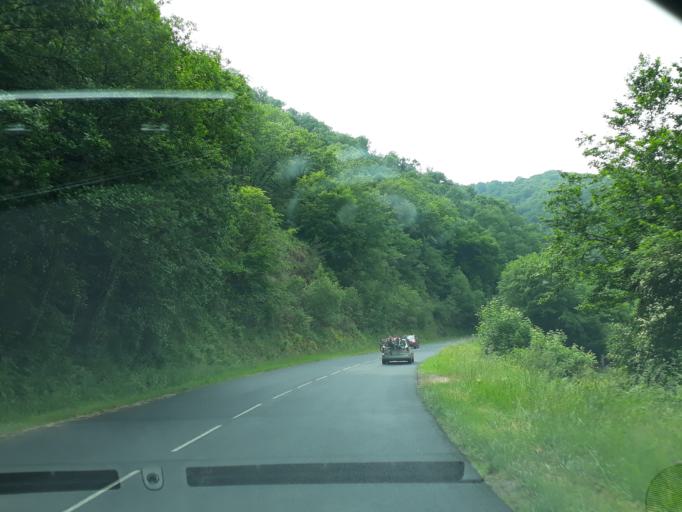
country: FR
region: Limousin
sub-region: Departement de la Correze
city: Beynat
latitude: 45.1307
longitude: 1.6790
